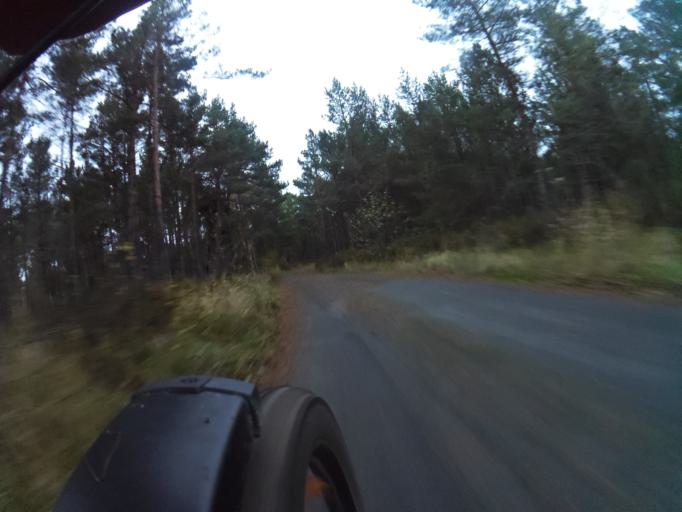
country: PL
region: Pomeranian Voivodeship
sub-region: Powiat wejherowski
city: Choczewo
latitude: 54.8008
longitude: 17.7832
